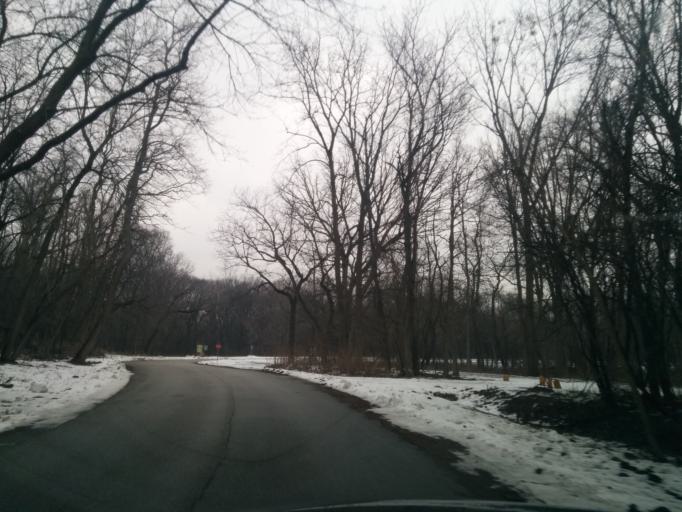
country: US
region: Illinois
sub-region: Cook County
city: Westchester
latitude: 41.8438
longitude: -87.8773
